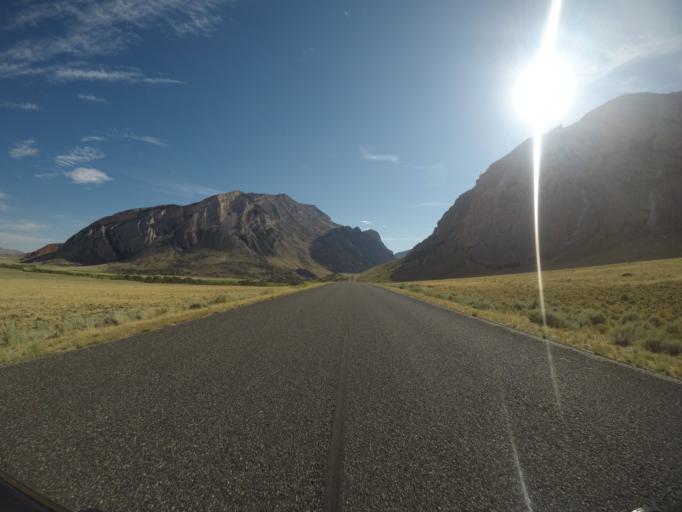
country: US
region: Montana
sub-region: Carbon County
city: Red Lodge
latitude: 44.8594
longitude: -109.2910
